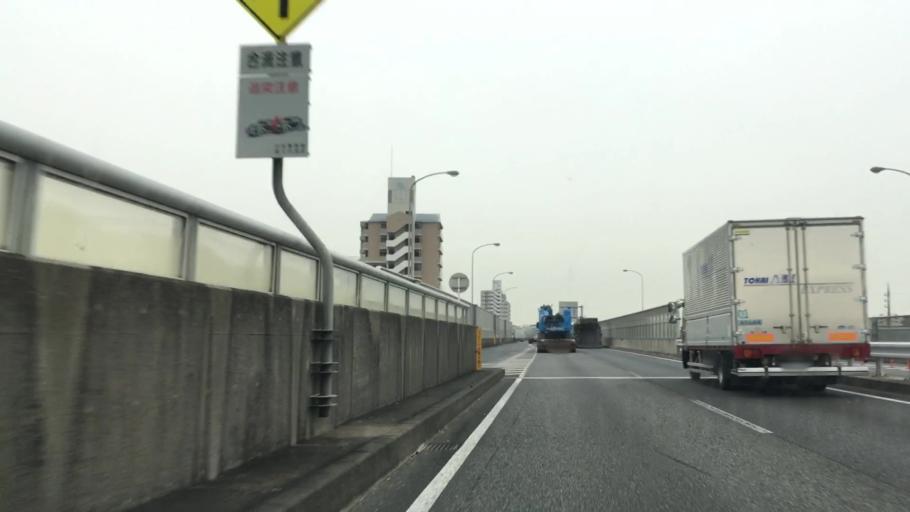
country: JP
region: Aichi
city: Chiryu
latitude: 34.9759
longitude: 137.0357
